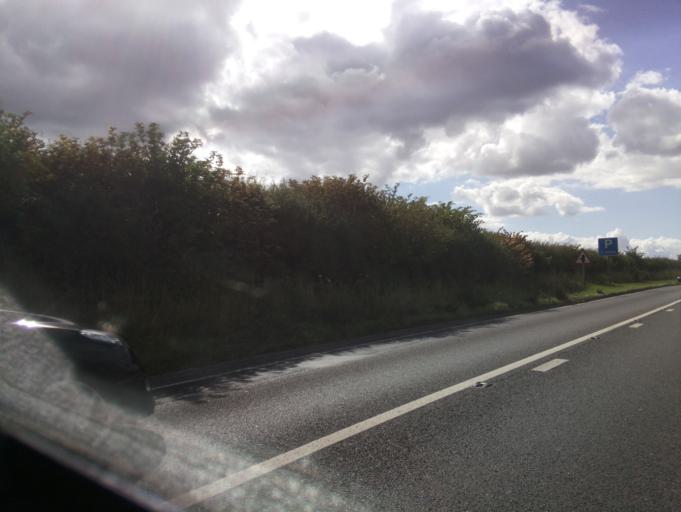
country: GB
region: England
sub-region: Wiltshire
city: Winterbourne Stoke
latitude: 51.1695
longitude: -1.8770
